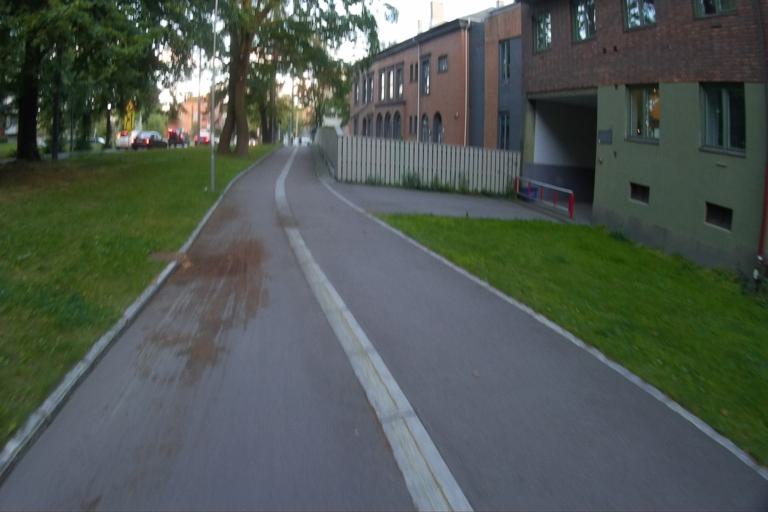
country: NO
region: Oslo
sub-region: Oslo
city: Oslo
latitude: 59.9300
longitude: 10.7671
